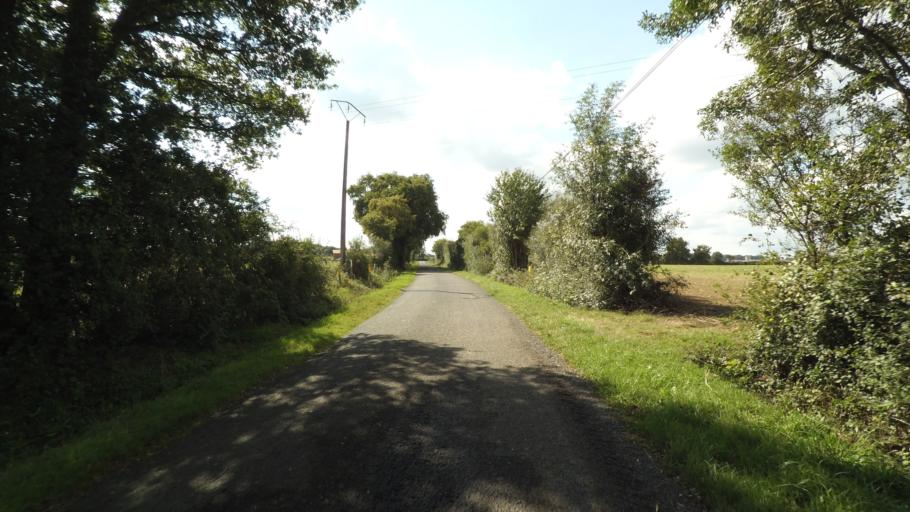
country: FR
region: Pays de la Loire
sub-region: Departement de la Vendee
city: Bouffere
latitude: 46.9636
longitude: -1.3799
